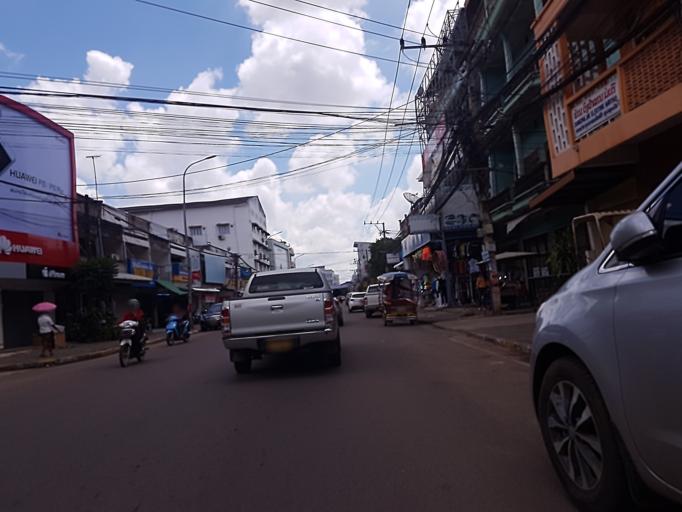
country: LA
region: Vientiane
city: Vientiane
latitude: 17.9610
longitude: 102.6225
